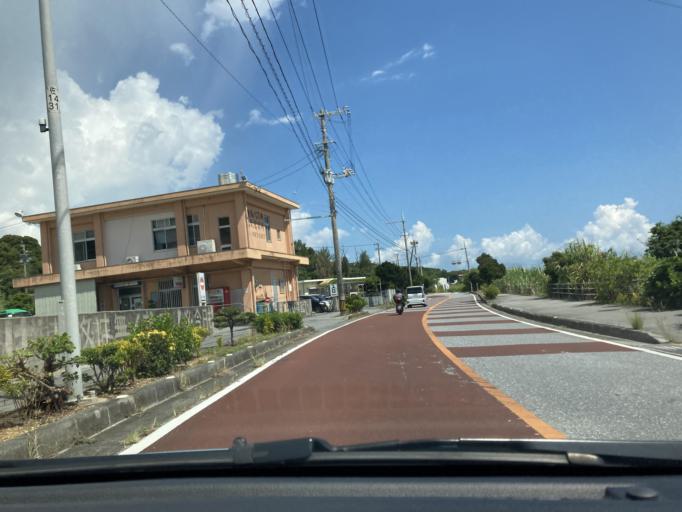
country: JP
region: Okinawa
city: Ginowan
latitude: 26.1770
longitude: 127.7674
